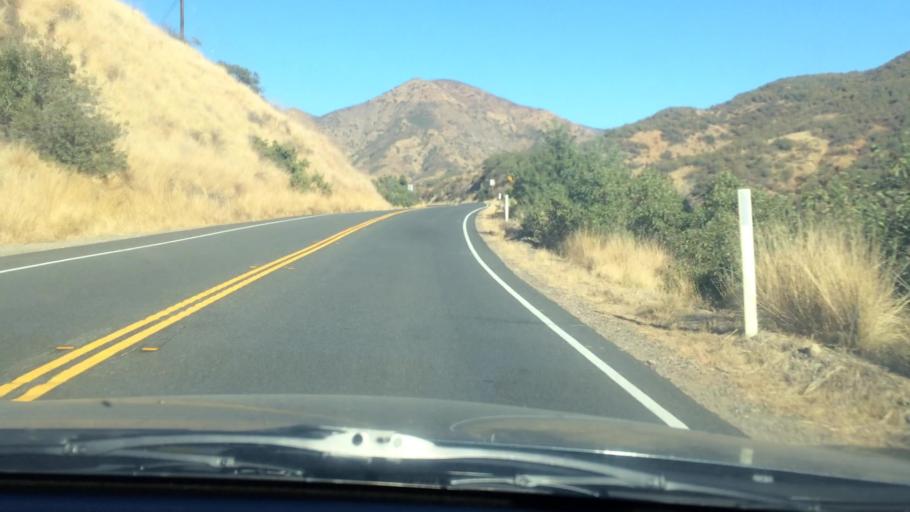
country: US
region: California
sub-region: Orange County
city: Coto De Caza
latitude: 33.5835
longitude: -117.5236
